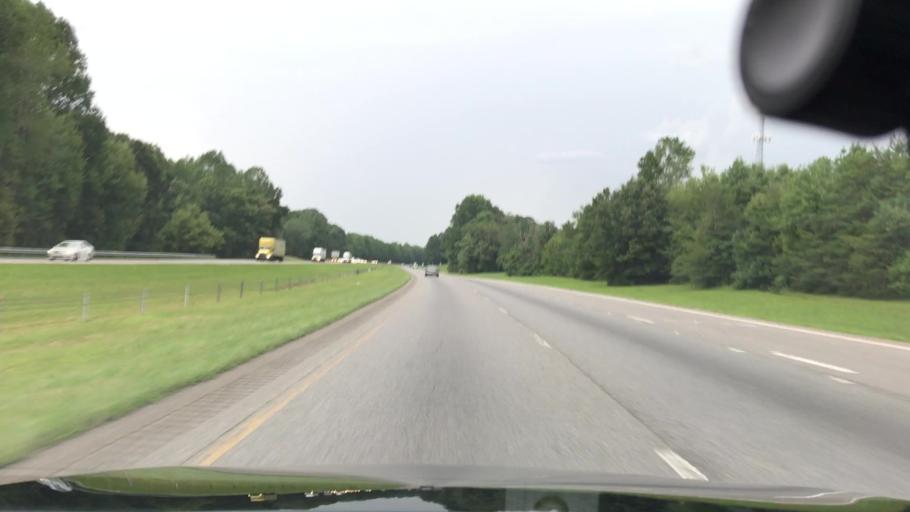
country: US
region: North Carolina
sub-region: Iredell County
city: Statesville
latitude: 35.8534
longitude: -80.8601
